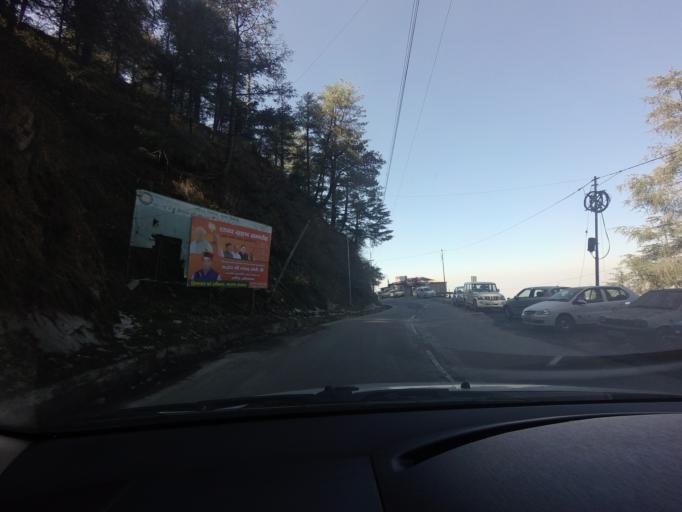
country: IN
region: Himachal Pradesh
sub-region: Shimla
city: Shimla
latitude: 31.1094
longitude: 77.2152
